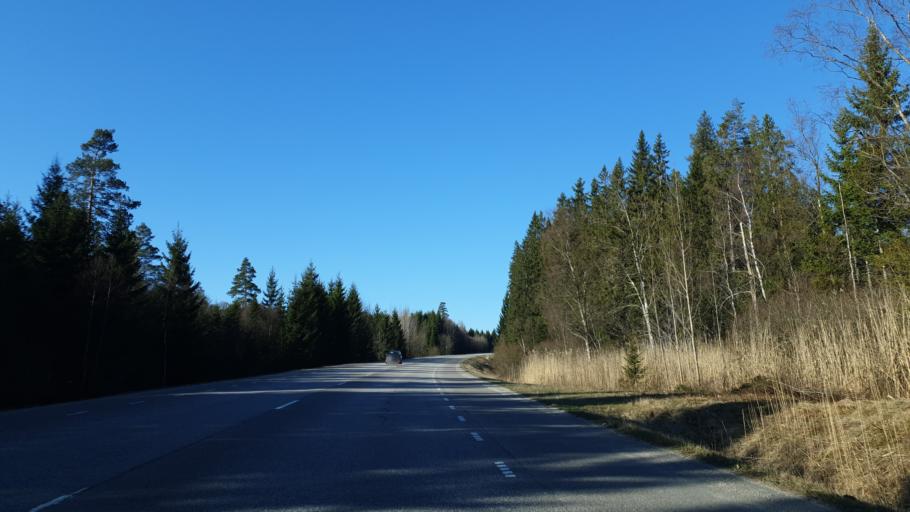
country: SE
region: Vaestra Goetaland
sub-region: Boras Kommun
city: Dalsjofors
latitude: 57.7596
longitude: 13.1103
